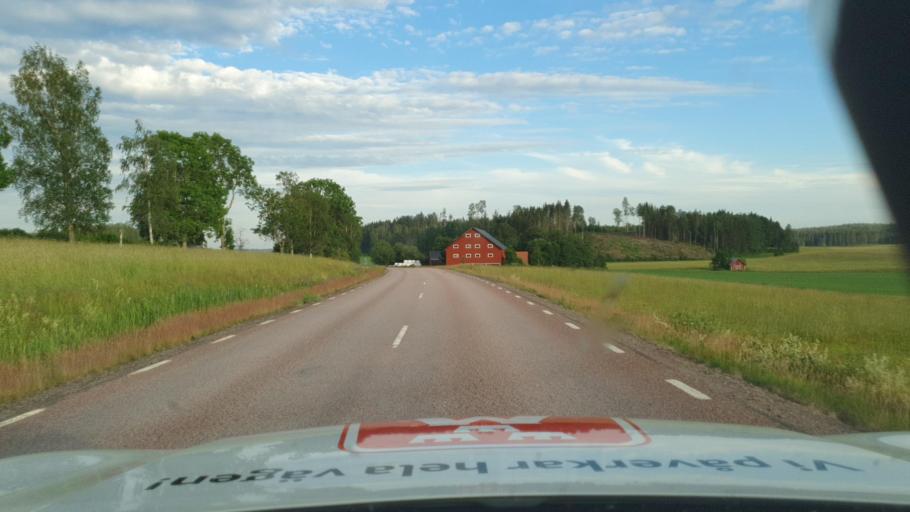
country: SE
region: Vaermland
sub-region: Karlstads Kommun
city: Molkom
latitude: 59.4705
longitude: 13.8099
